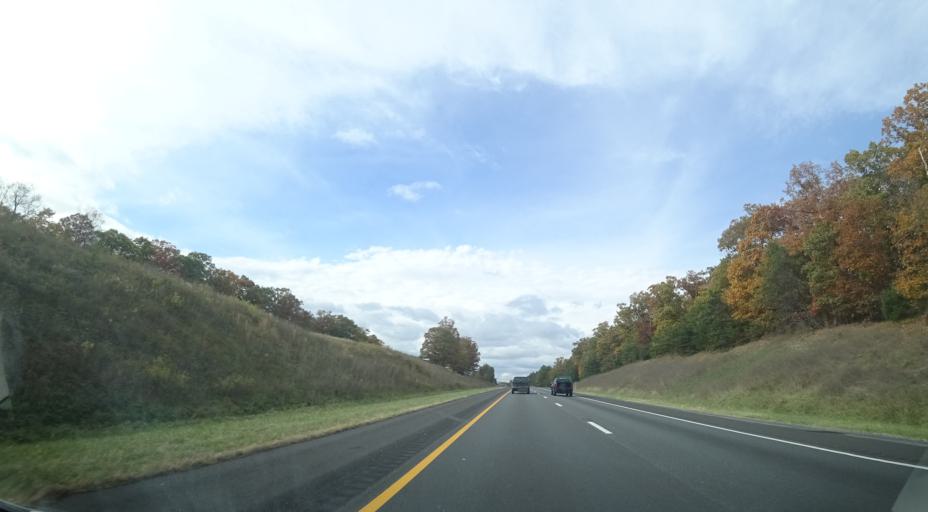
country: US
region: Virginia
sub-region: Warren County
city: Front Royal
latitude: 38.9679
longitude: -78.2034
